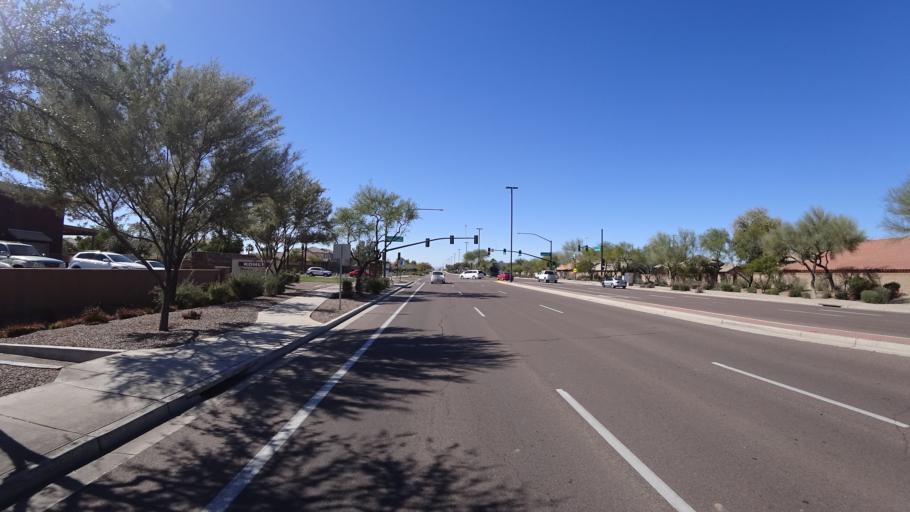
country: US
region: Arizona
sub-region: Maricopa County
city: Gilbert
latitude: 33.3066
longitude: -111.7597
